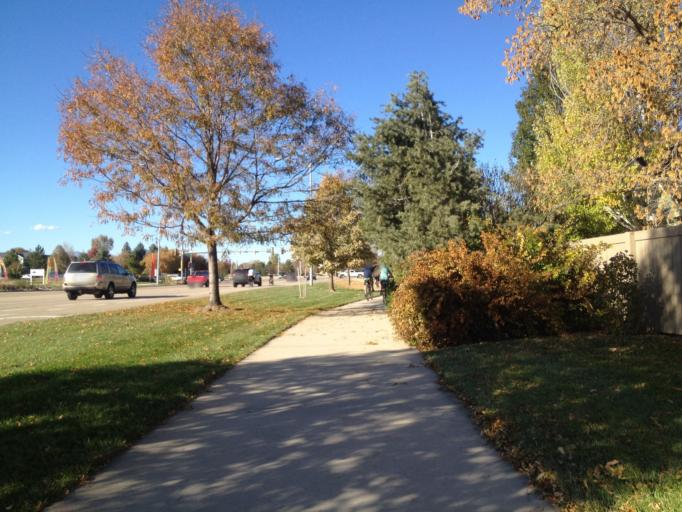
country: US
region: Colorado
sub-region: Boulder County
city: Niwot
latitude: 40.1420
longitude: -105.1496
